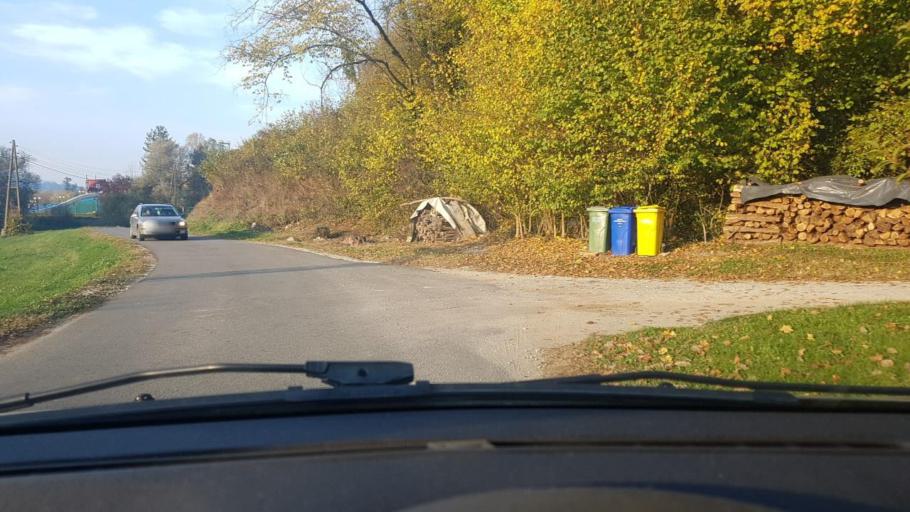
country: SI
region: Podcetrtek
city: Podcetrtek
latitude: 46.1633
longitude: 15.6068
